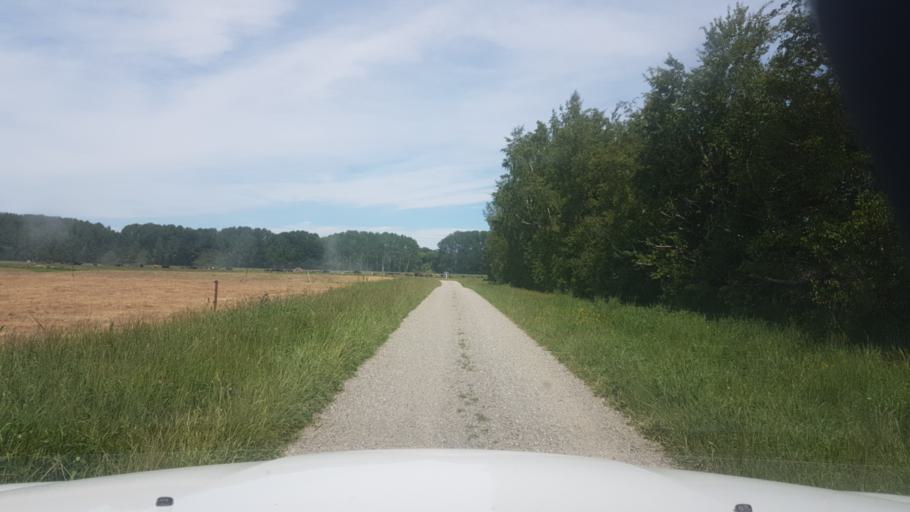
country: NZ
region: Canterbury
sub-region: Timaru District
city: Pleasant Point
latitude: -44.2224
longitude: 171.1204
